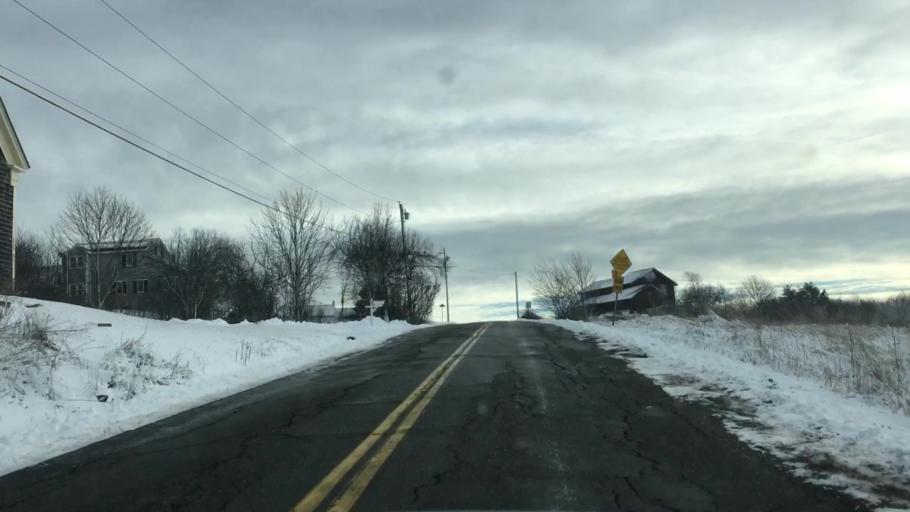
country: US
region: Maine
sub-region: Knox County
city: Rockland
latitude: 44.1116
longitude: -69.1285
